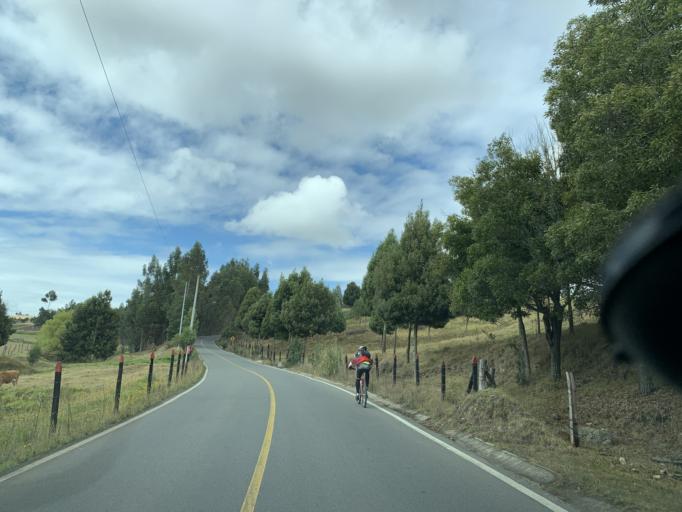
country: CO
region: Boyaca
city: Siachoque
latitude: 5.5681
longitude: -73.2399
